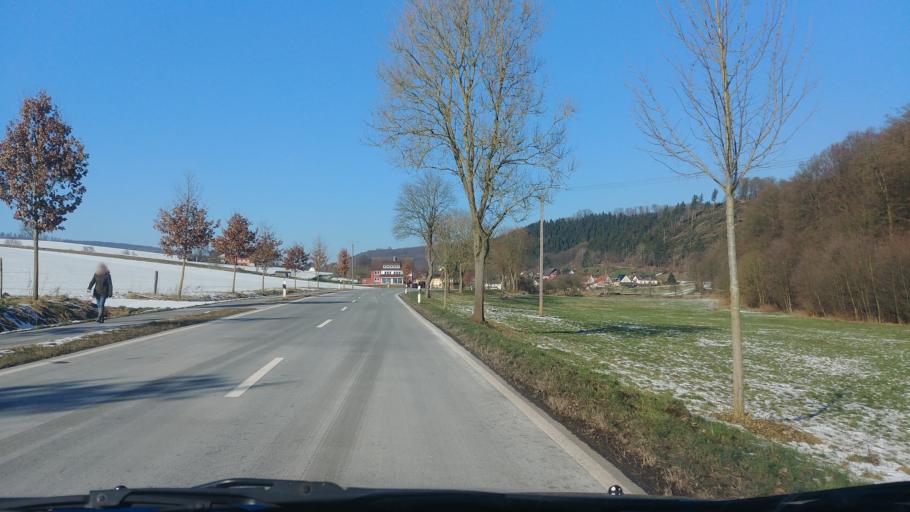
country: DE
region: Lower Saxony
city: Hardegsen
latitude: 51.6754
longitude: 9.7454
